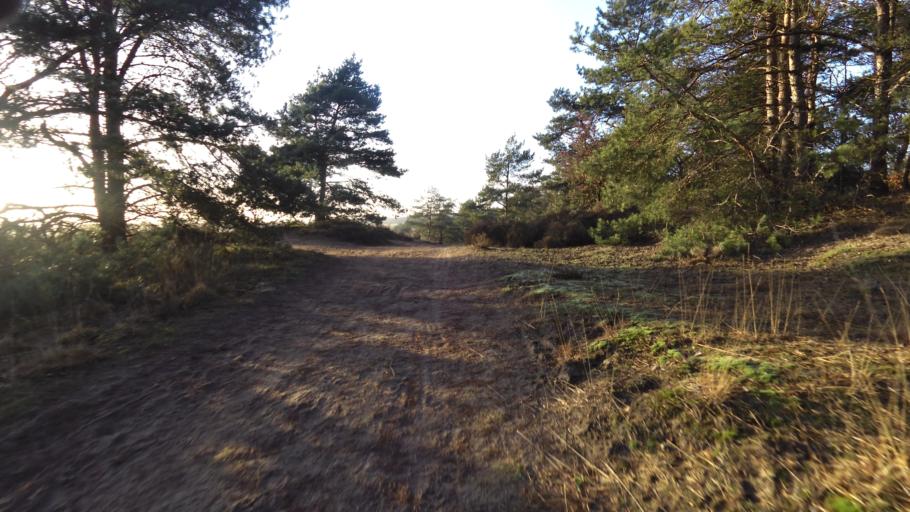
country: NL
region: Gelderland
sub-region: Gemeente Apeldoorn
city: Uddel
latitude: 52.2162
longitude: 5.8525
